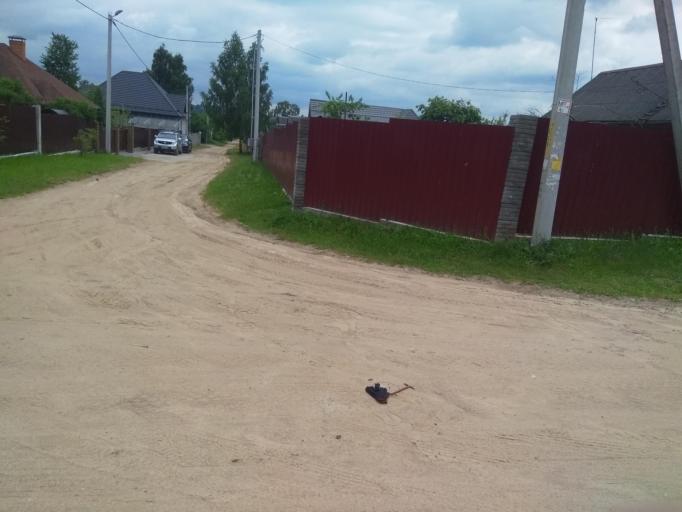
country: BY
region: Mogilev
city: Mahilyow
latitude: 53.9052
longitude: 30.3952
